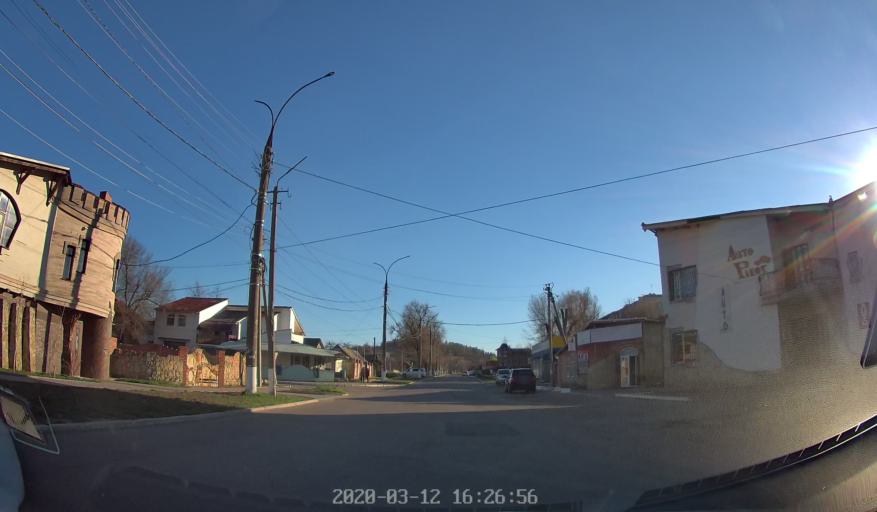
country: MD
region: Anenii Noi
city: Anenii Noi
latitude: 46.8787
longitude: 29.2319
